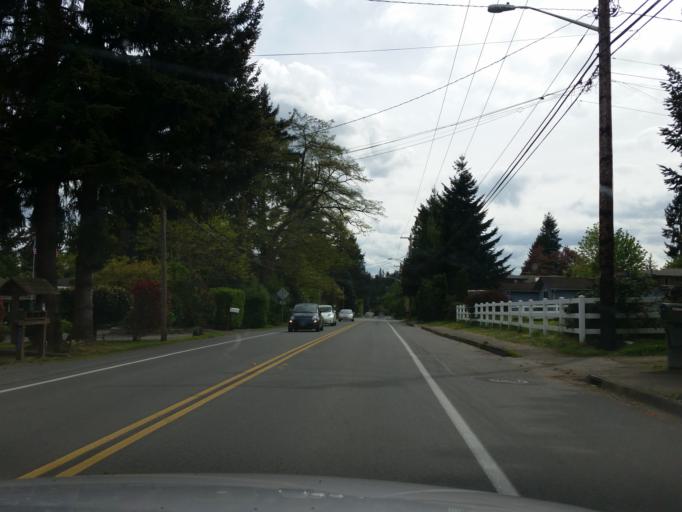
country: US
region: Washington
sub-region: King County
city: Kingsgate
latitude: 47.6929
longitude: -122.1649
